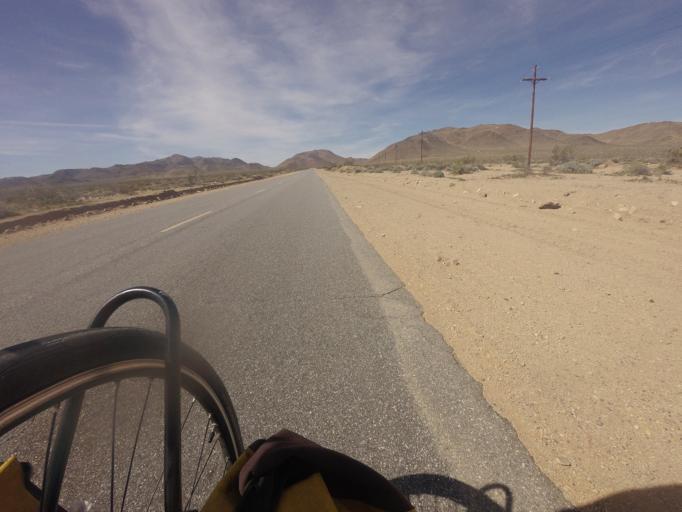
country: US
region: California
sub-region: San Bernardino County
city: Searles Valley
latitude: 35.5718
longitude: -117.4456
